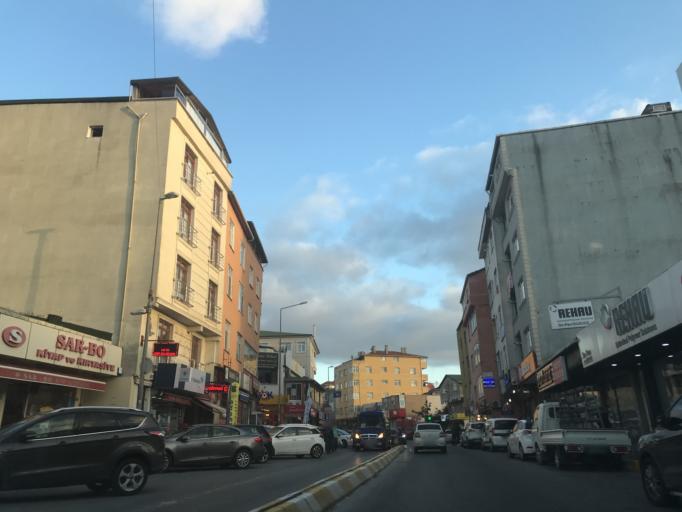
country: TR
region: Istanbul
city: Sisli
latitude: 41.1312
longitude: 29.0411
